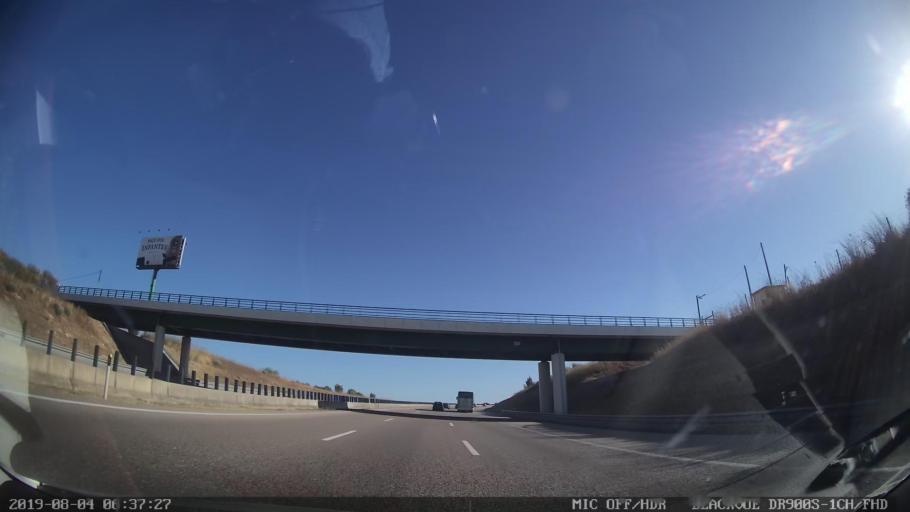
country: PT
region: Santarem
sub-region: Alcanena
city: Alcanena
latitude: 39.3669
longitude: -8.6300
